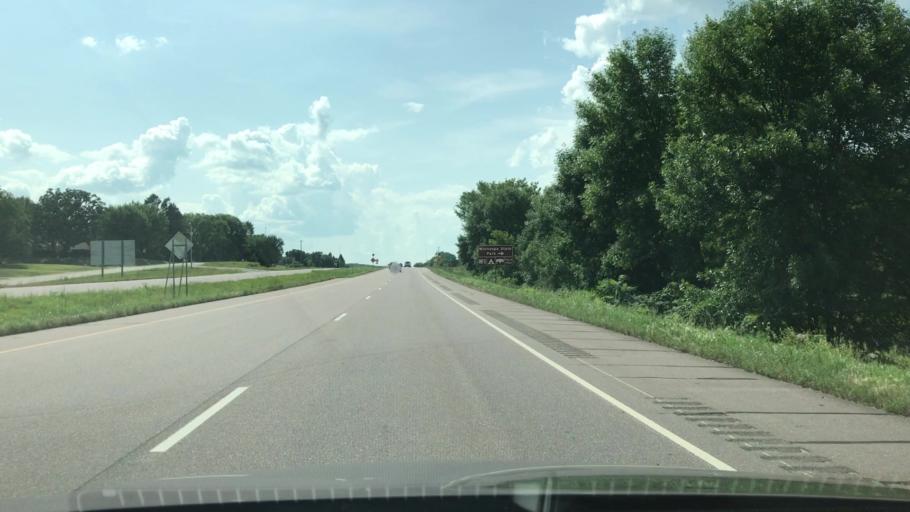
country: US
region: Minnesota
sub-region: Nicollet County
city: North Mankato
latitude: 44.1524
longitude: -94.0568
